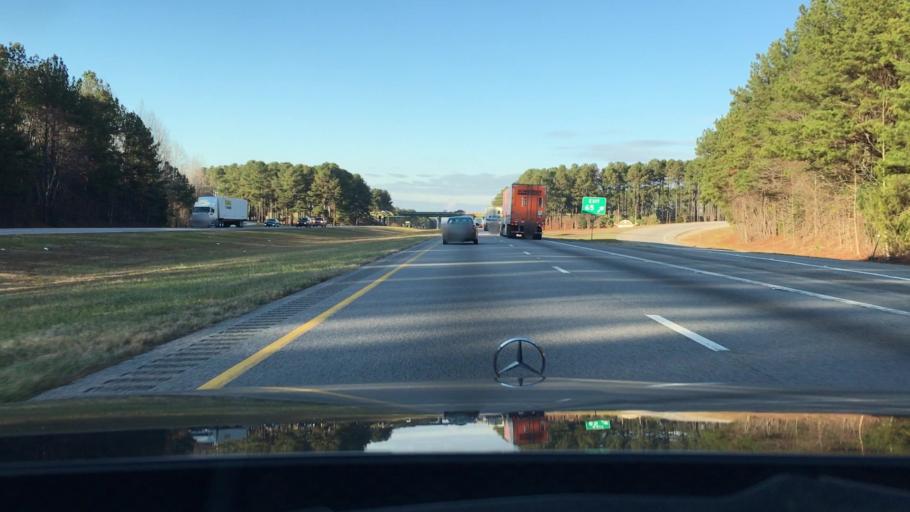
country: US
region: South Carolina
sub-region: Chester County
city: Eureka Mill
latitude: 34.7415
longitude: -81.0350
